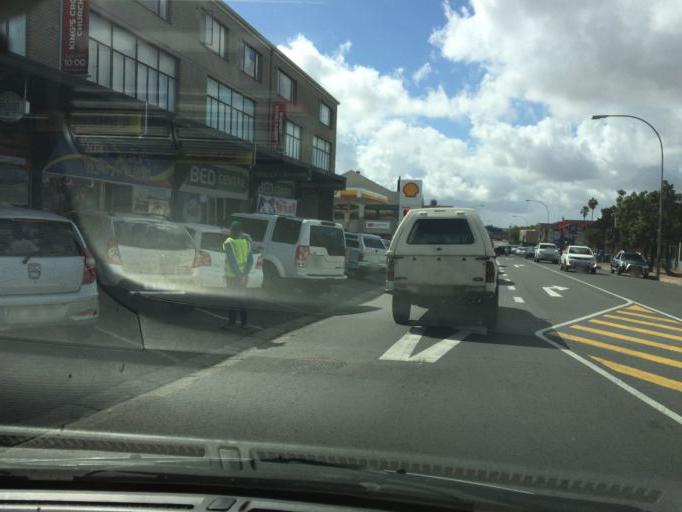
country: ZA
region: Western Cape
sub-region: City of Cape Town
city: Kraaifontein
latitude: -33.8302
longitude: 18.6492
